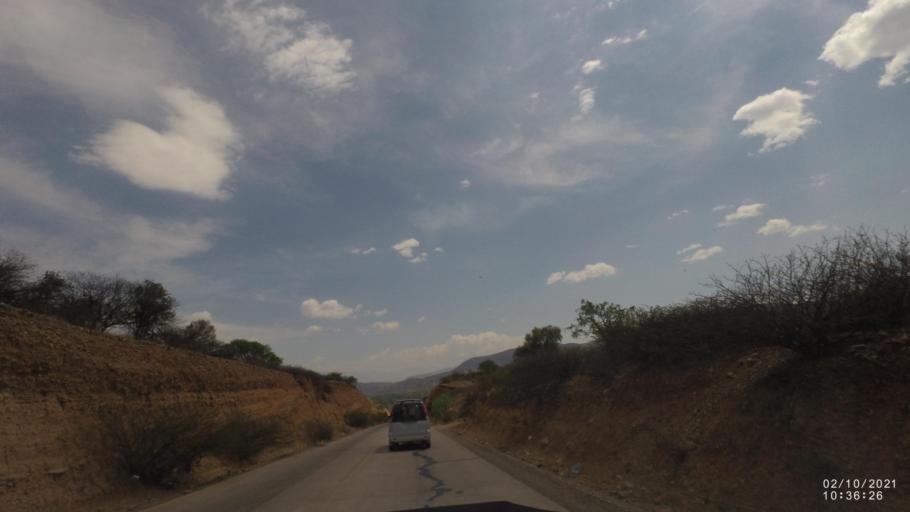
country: BO
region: Cochabamba
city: Capinota
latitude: -17.6507
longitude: -66.2585
